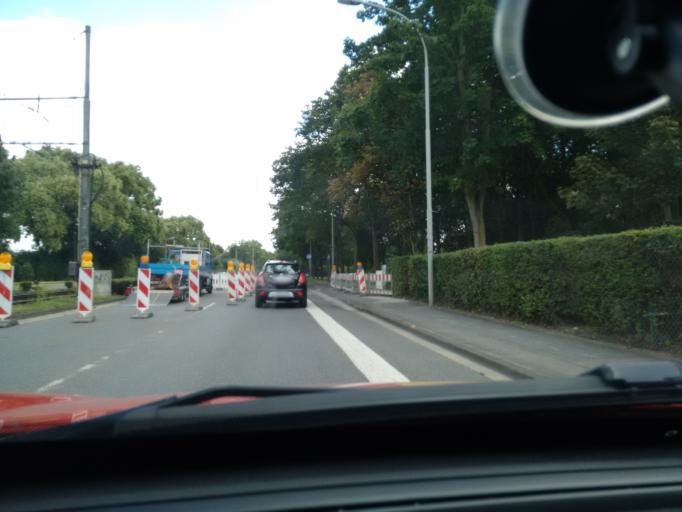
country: DE
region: Rheinland-Pfalz
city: Mainz
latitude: 49.9849
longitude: 8.2670
